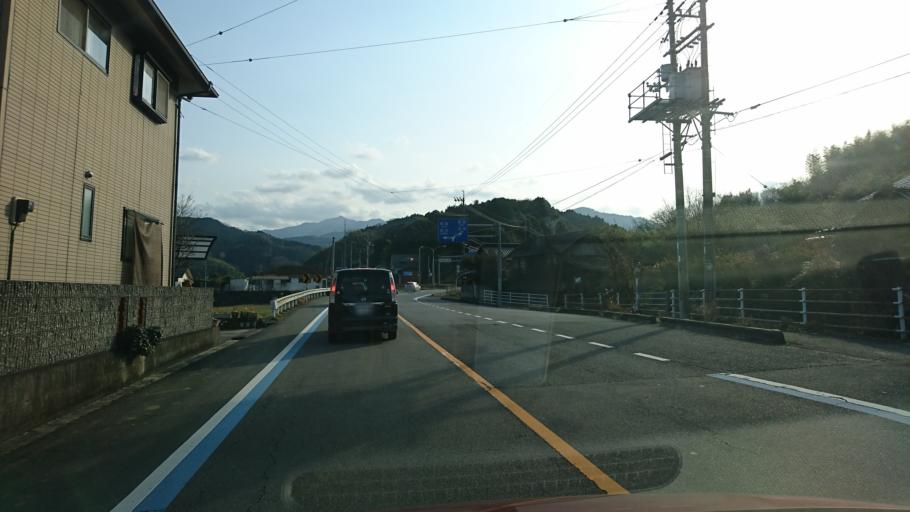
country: JP
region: Ehime
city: Hojo
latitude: 34.0030
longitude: 132.9380
